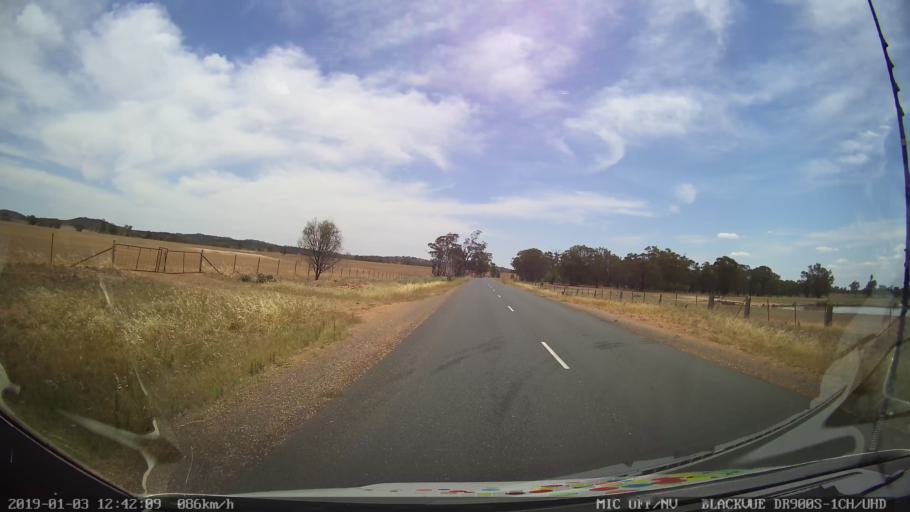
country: AU
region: New South Wales
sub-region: Weddin
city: Grenfell
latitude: -33.7906
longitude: 148.2130
